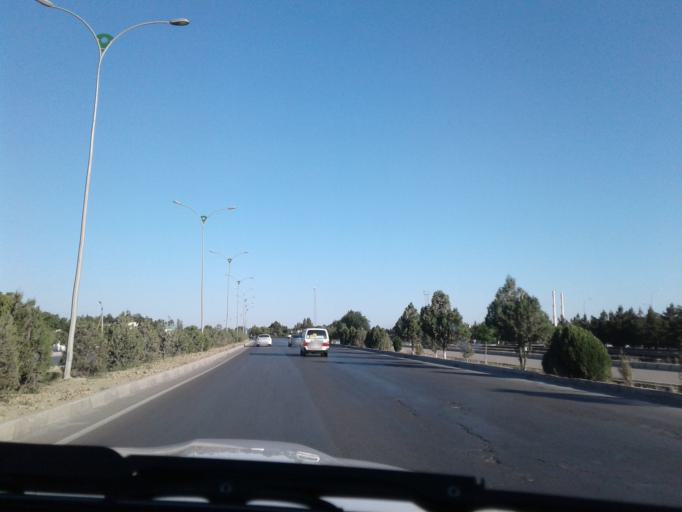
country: TM
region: Ahal
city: Abadan
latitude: 38.1554
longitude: 57.9740
